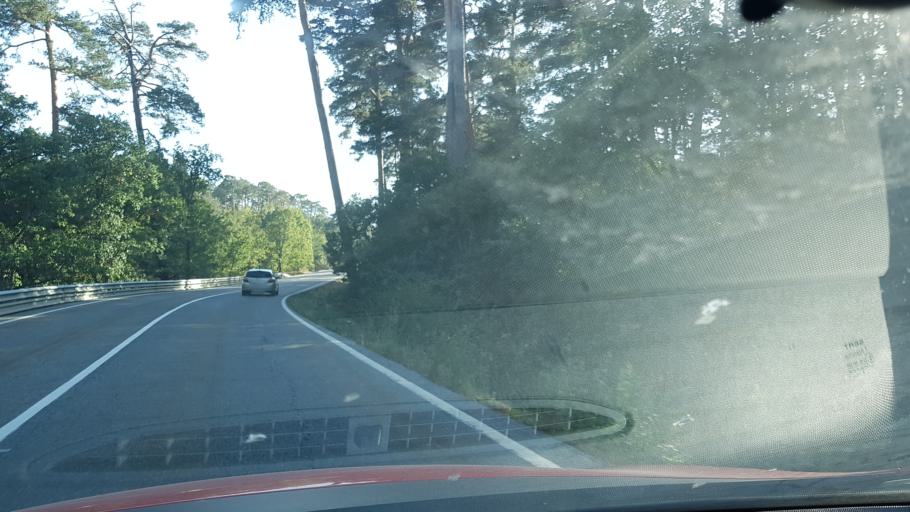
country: ES
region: Castille and Leon
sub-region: Provincia de Segovia
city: San Ildefonso
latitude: 40.8592
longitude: -4.0262
